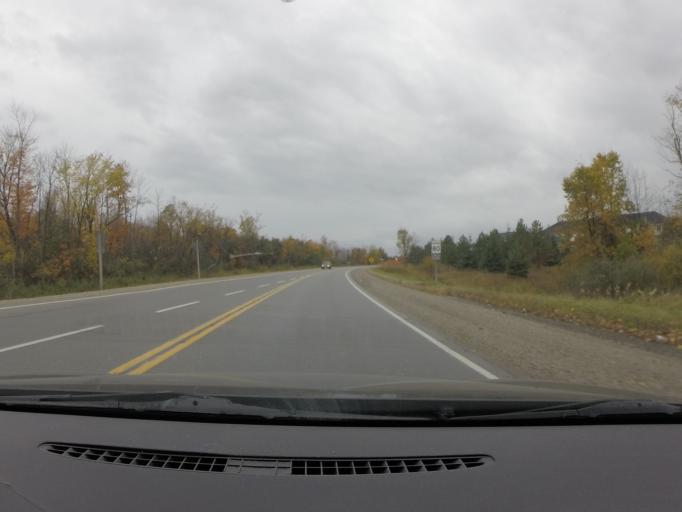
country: CA
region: Ontario
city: Carleton Place
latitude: 45.1233
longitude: -76.1363
